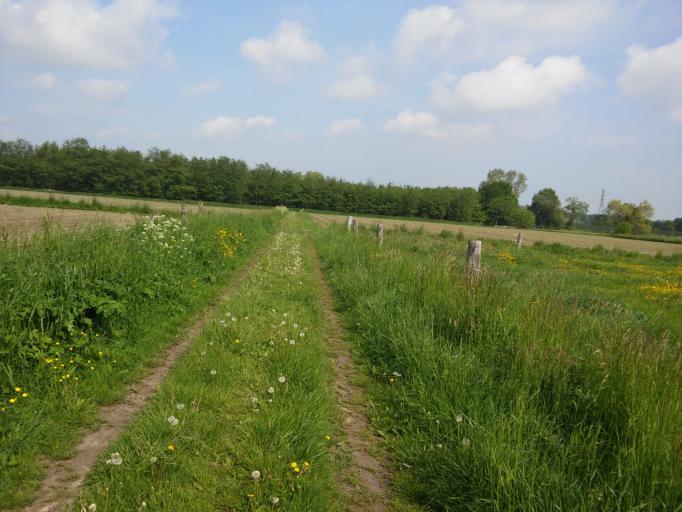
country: BE
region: Flanders
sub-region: Provincie Antwerpen
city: Mechelen
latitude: 51.0249
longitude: 4.4350
